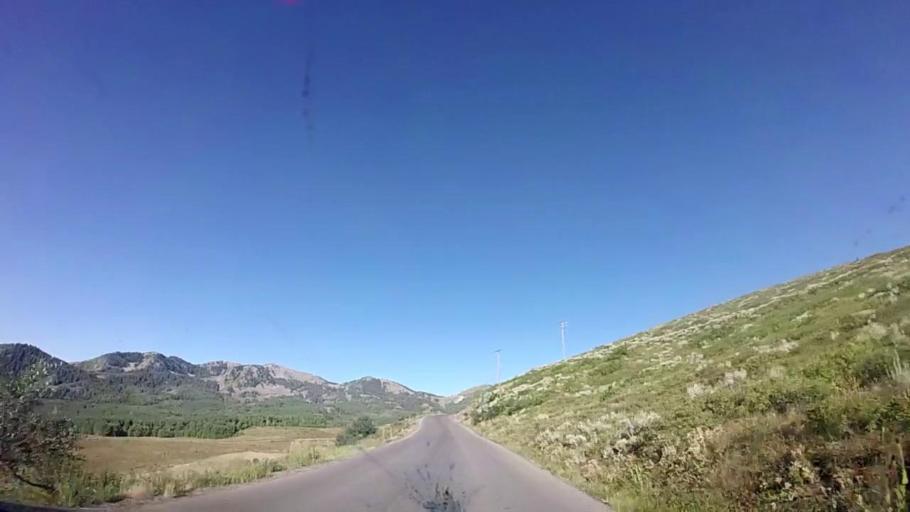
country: US
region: Utah
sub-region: Summit County
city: Park City
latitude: 40.6058
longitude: -111.5120
